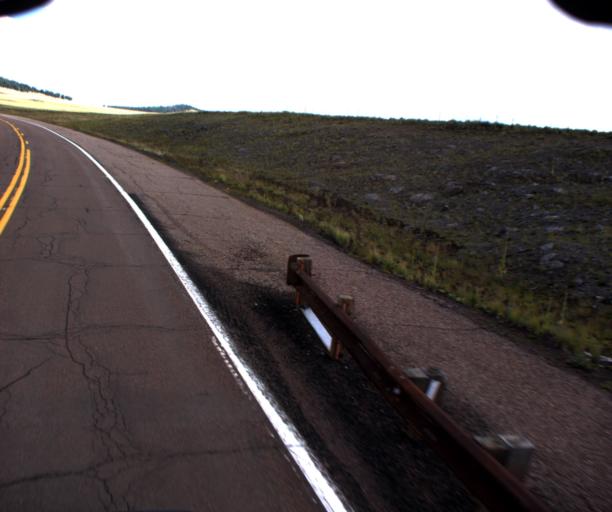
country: US
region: Arizona
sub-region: Apache County
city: Eagar
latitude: 34.0516
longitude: -109.5440
